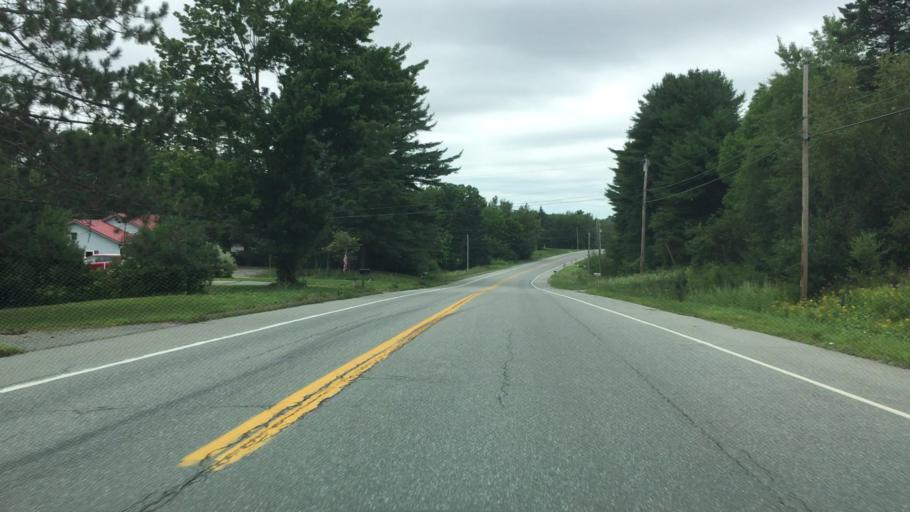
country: US
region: Maine
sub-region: Waldo County
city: Winterport
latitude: 44.6794
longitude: -68.8427
